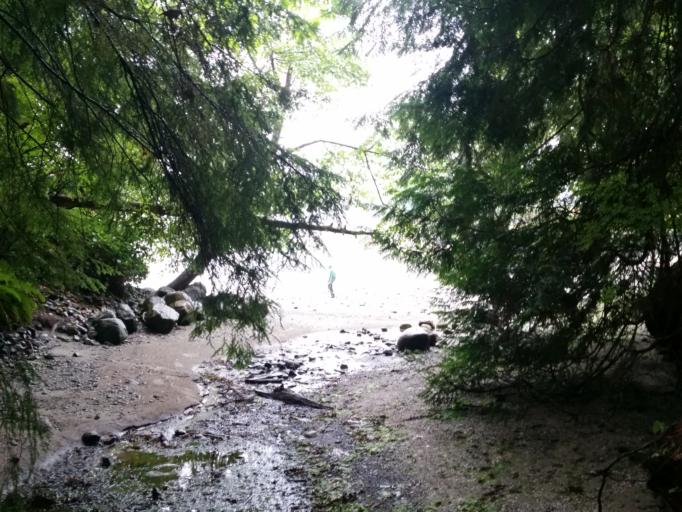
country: CA
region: British Columbia
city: Burnaby
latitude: 49.3119
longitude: -122.9266
